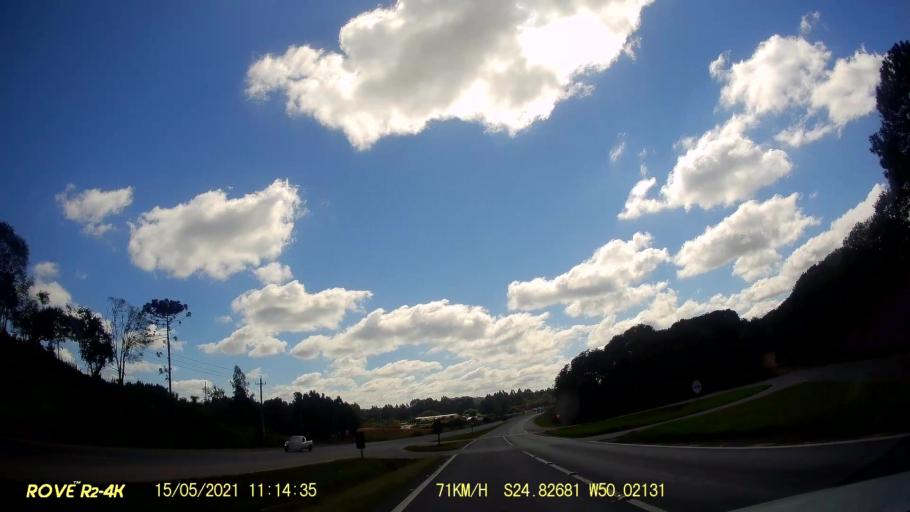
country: BR
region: Parana
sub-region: Castro
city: Castro
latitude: -24.8269
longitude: -50.0213
